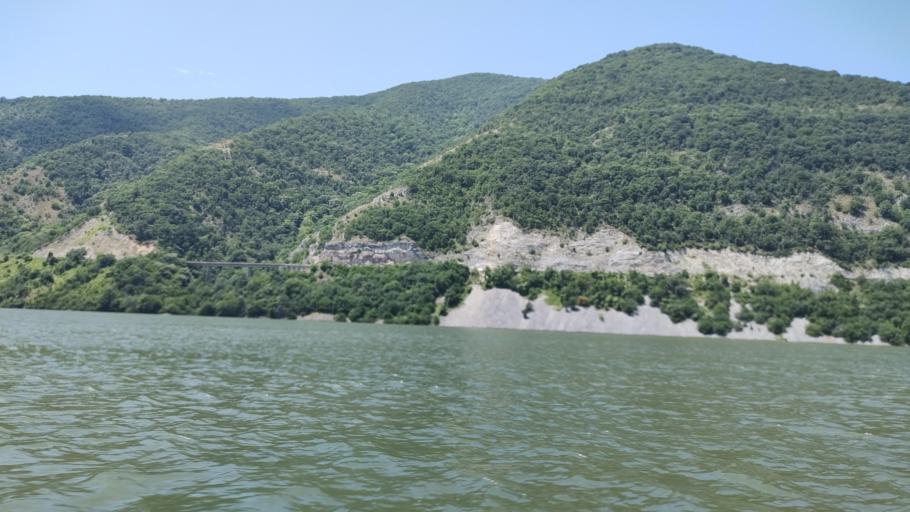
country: RO
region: Caras-Severin
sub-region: Comuna Berzasca
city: Berzasca
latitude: 44.5844
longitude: 22.0271
